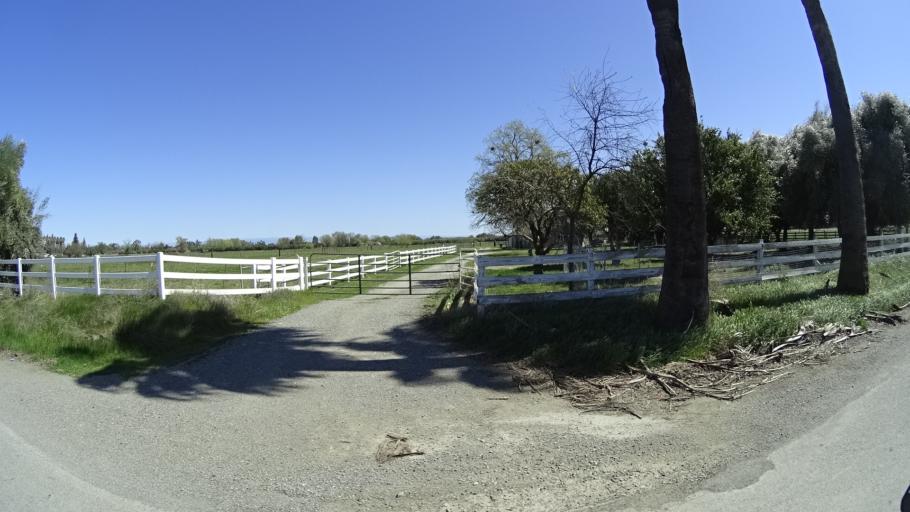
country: US
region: California
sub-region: Glenn County
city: Orland
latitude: 39.7682
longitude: -122.2478
